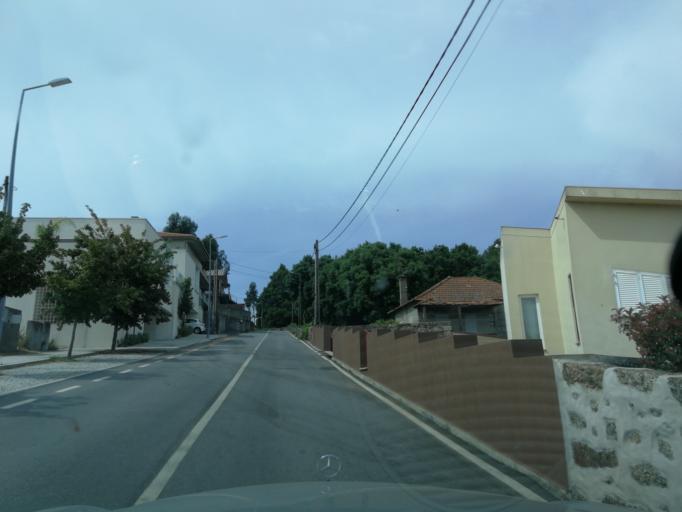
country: PT
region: Braga
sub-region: Vila Nova de Famalicao
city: Calendario
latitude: 41.4082
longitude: -8.5329
